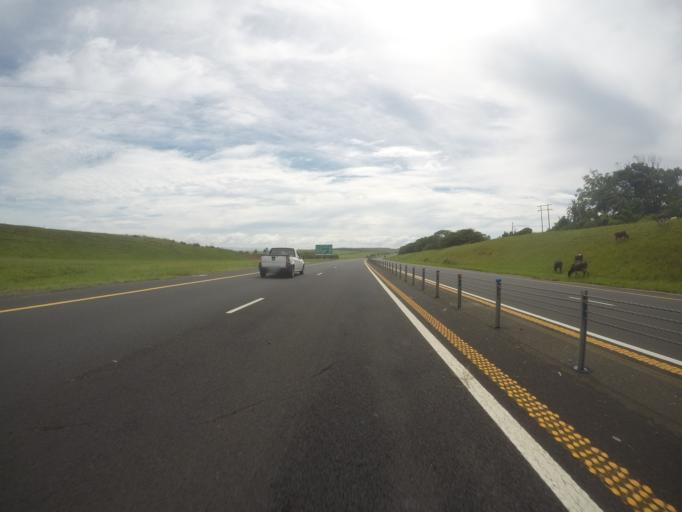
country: ZA
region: KwaZulu-Natal
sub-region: iLembe District Municipality
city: Mandeni
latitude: -29.0577
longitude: 31.6293
